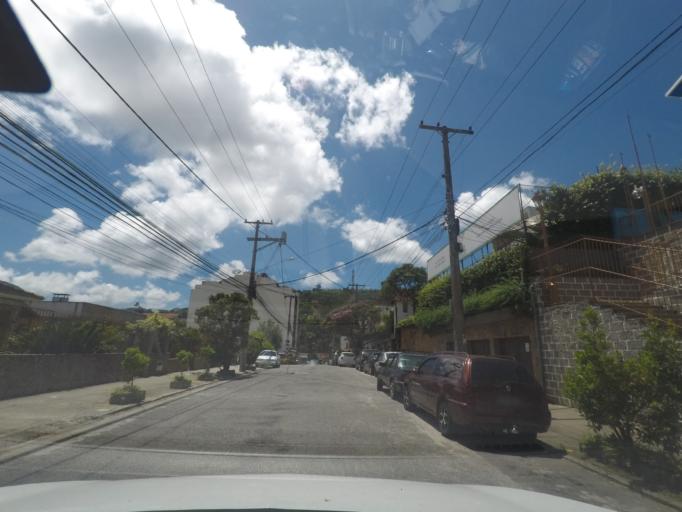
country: BR
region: Rio de Janeiro
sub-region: Teresopolis
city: Teresopolis
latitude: -22.4223
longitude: -42.9787
